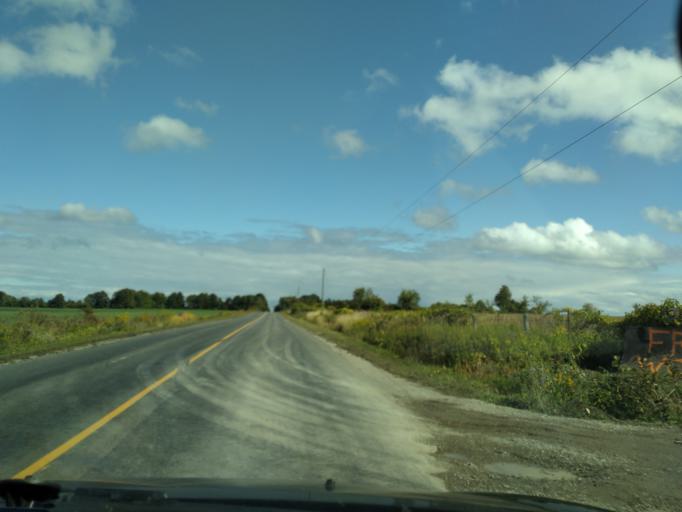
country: CA
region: Ontario
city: Innisfil
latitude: 44.2823
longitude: -79.5808
